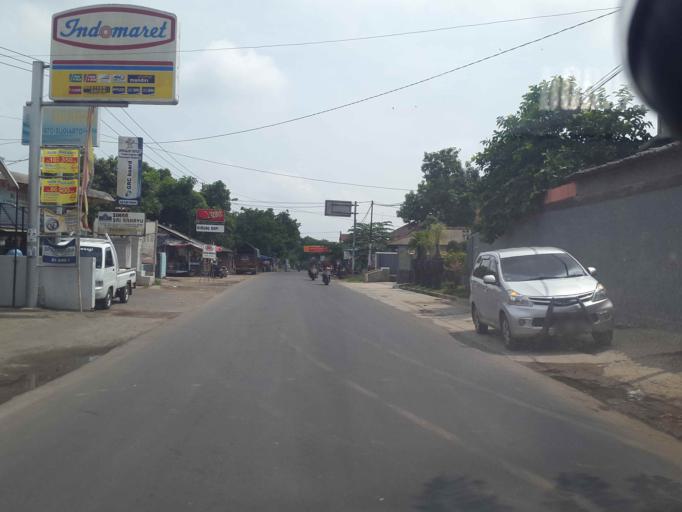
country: ID
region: West Java
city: Rengasdengklok
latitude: -6.2920
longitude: 107.3654
